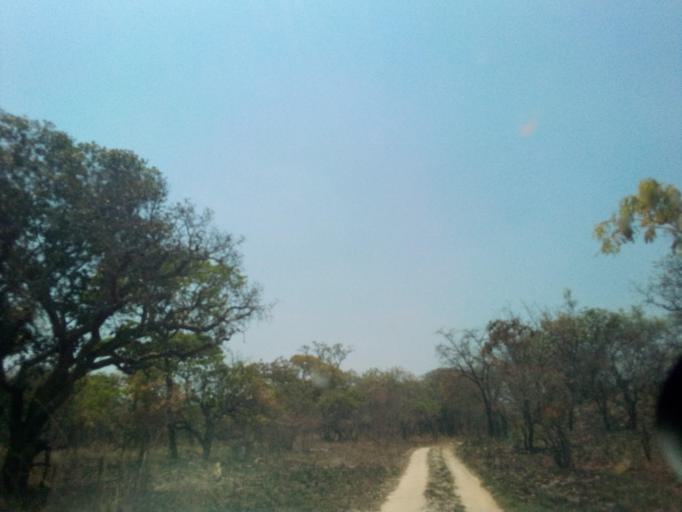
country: ZM
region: Copperbelt
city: Kataba
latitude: -12.2378
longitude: 30.4051
